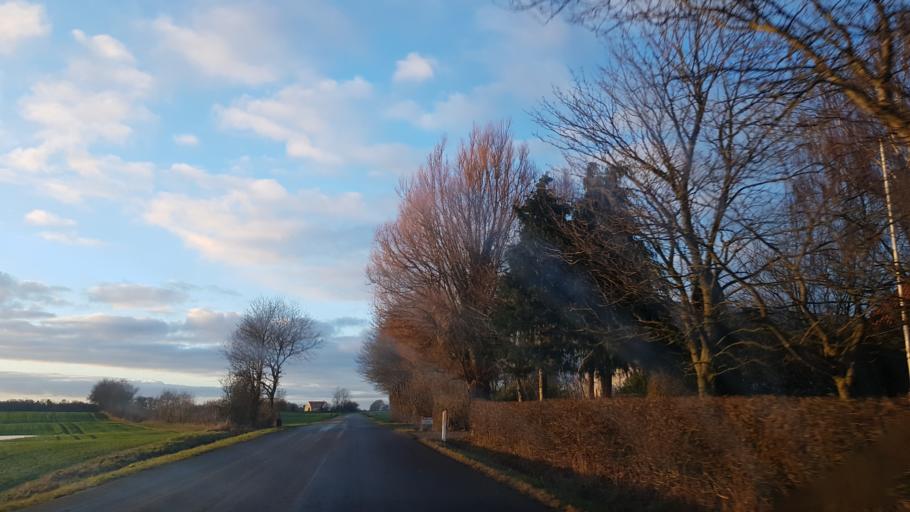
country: DK
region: South Denmark
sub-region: Kolding Kommune
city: Vamdrup
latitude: 55.3675
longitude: 9.3160
